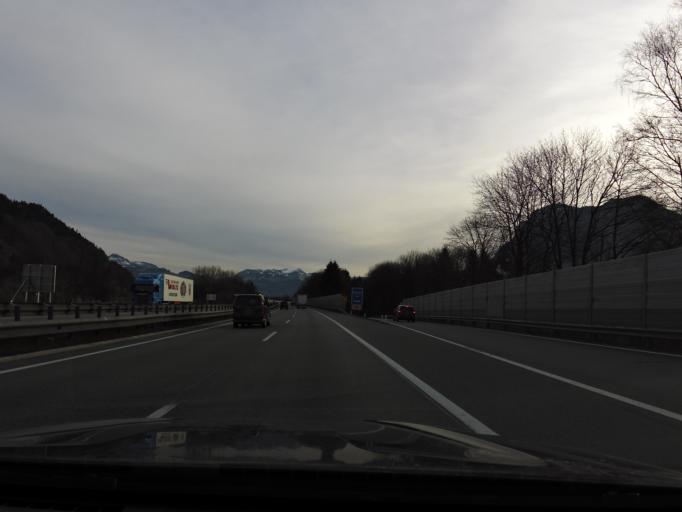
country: AT
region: Tyrol
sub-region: Politischer Bezirk Kufstein
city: Kufstein
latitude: 47.5946
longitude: 12.1732
